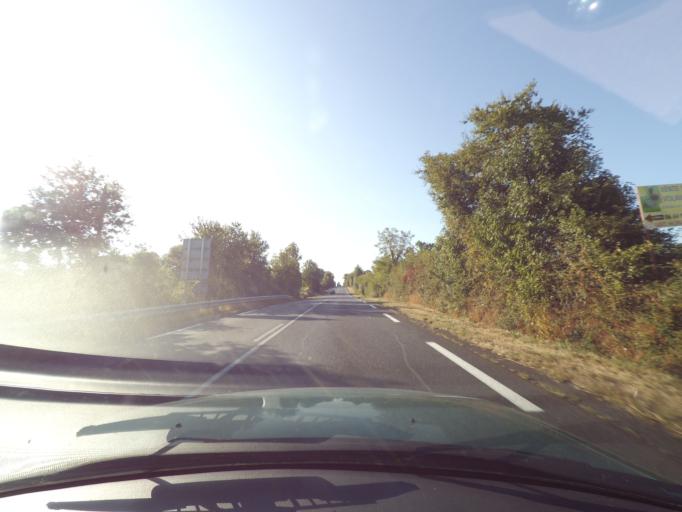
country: FR
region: Poitou-Charentes
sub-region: Departement des Deux-Sevres
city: Chiche
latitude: 46.7841
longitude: -0.3366
